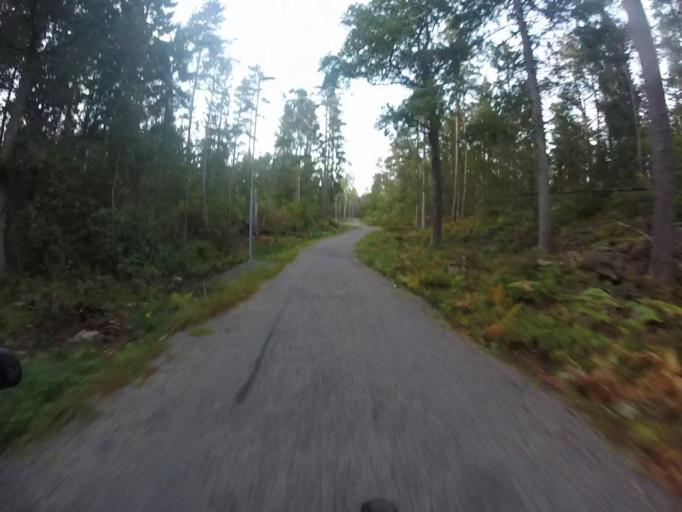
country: SE
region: Vaestra Goetaland
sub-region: Trollhattan
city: Trollhattan
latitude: 58.2957
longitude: 12.2695
